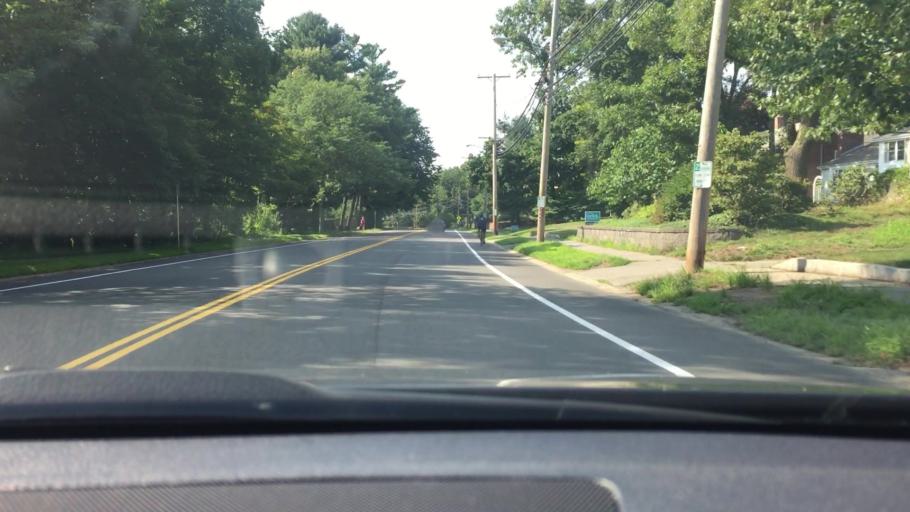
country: US
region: Massachusetts
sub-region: Norfolk County
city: Needham
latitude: 42.2737
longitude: -71.2128
